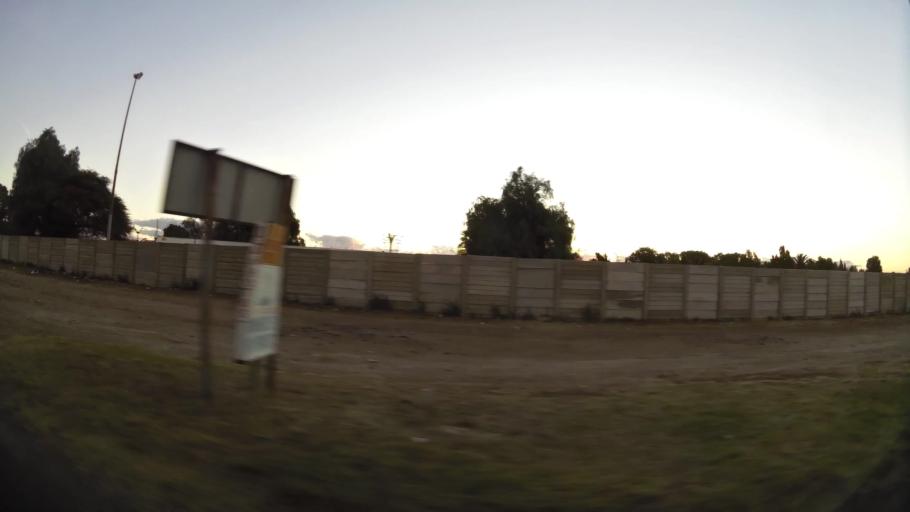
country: ZA
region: Northern Cape
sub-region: Frances Baard District Municipality
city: Kimberley
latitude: -28.7144
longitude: 24.7721
